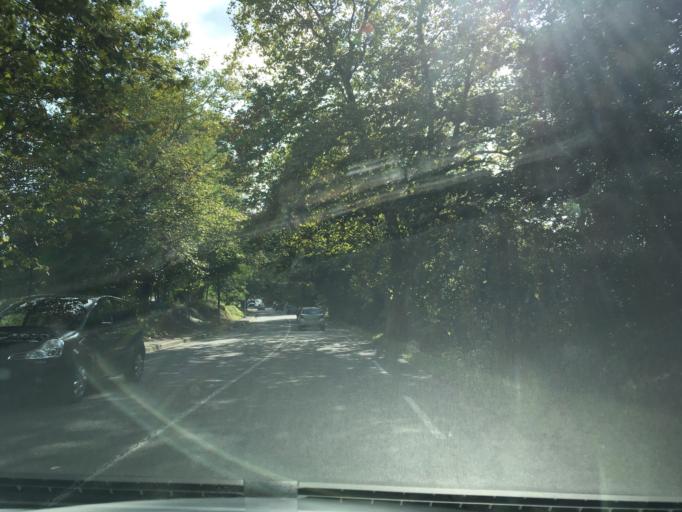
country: FR
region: Aquitaine
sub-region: Departement des Pyrenees-Atlantiques
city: Bayonne
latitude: 43.4721
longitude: -1.4867
